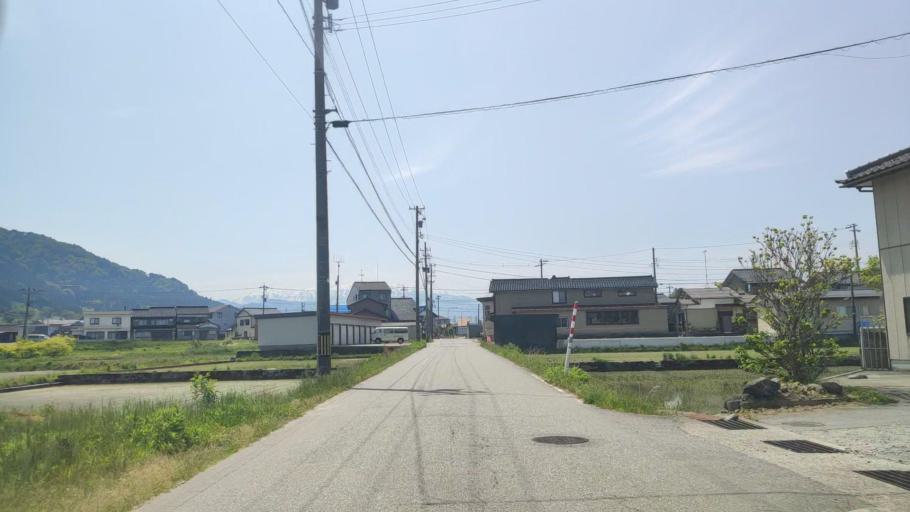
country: JP
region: Toyama
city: Nyuzen
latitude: 36.9589
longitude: 137.5680
